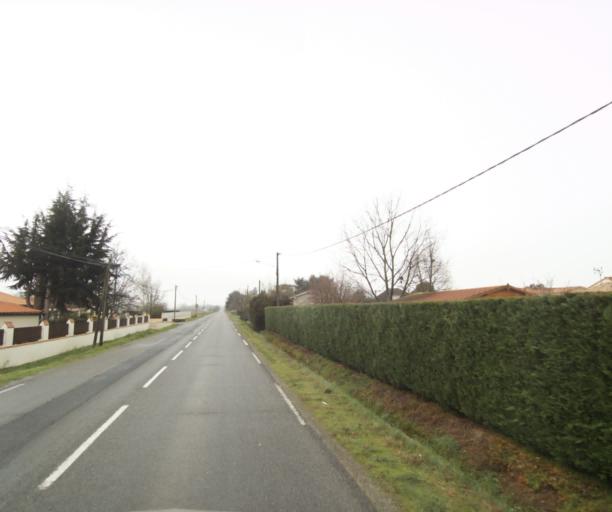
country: FR
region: Midi-Pyrenees
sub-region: Departement de la Haute-Garonne
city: Villemur-sur-Tarn
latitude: 43.8570
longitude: 1.4784
